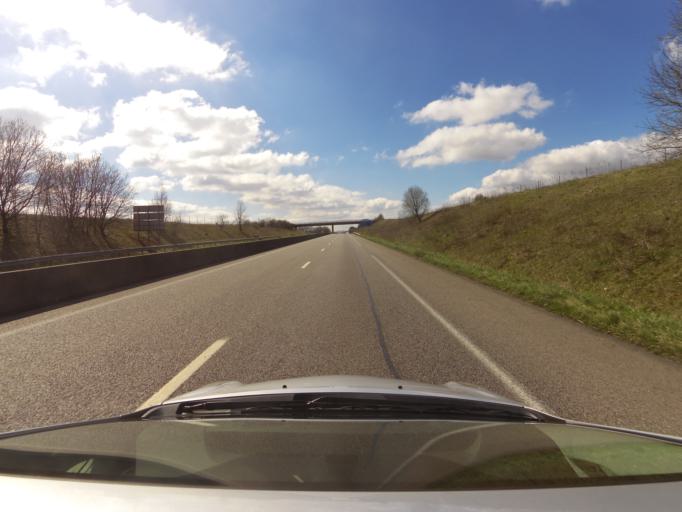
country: FR
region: Haute-Normandie
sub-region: Departement de la Seine-Maritime
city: Foucarmont
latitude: 49.8221
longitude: 1.5186
